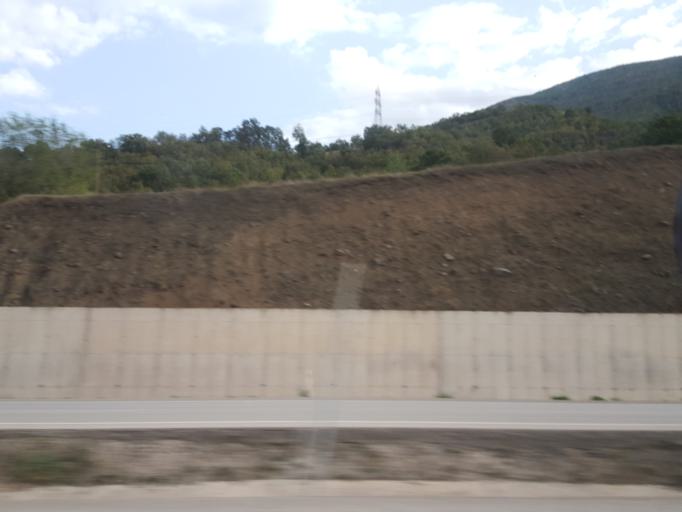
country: TR
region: Tokat
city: Basciftlik
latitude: 40.4174
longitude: 37.1916
